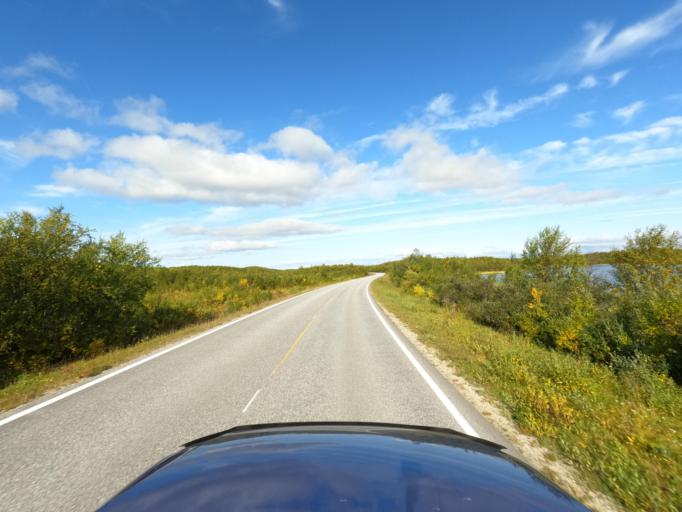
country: NO
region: Finnmark Fylke
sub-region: Karasjok
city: Karasjohka
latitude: 69.5964
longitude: 25.3296
